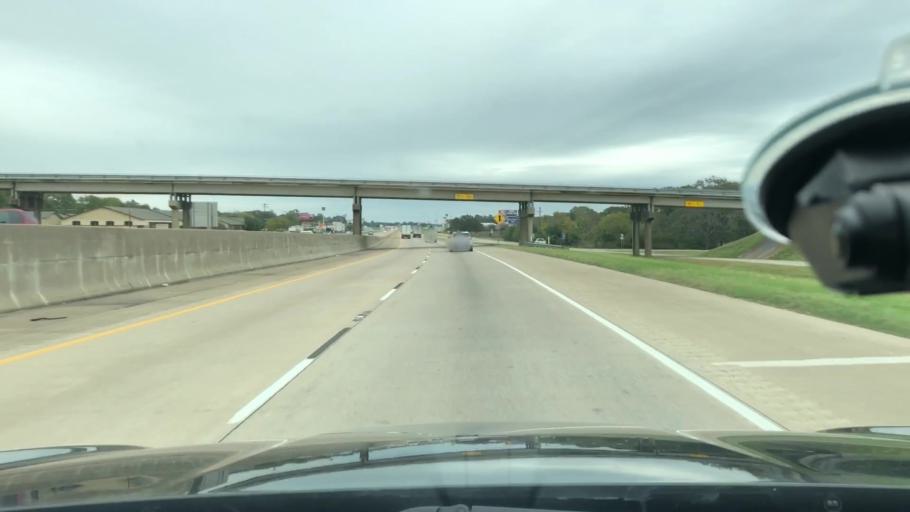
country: US
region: Texas
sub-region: Hopkins County
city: Sulphur Springs
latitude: 33.1163
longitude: -95.6138
